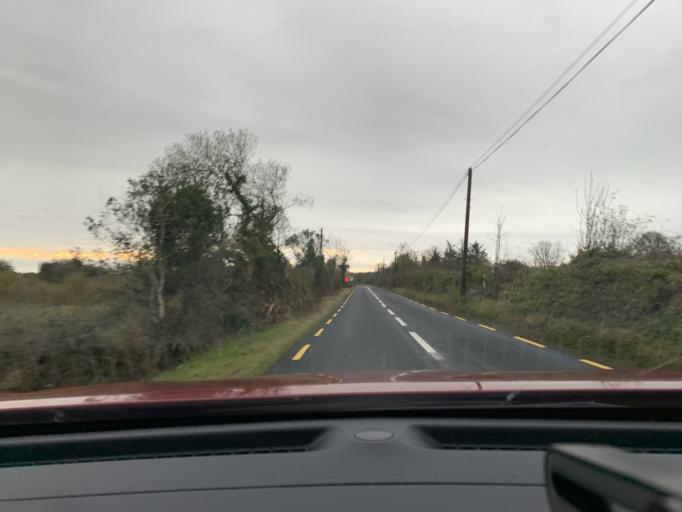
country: IE
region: Connaught
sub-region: Roscommon
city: Ballaghaderreen
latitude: 53.9299
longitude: -8.5312
